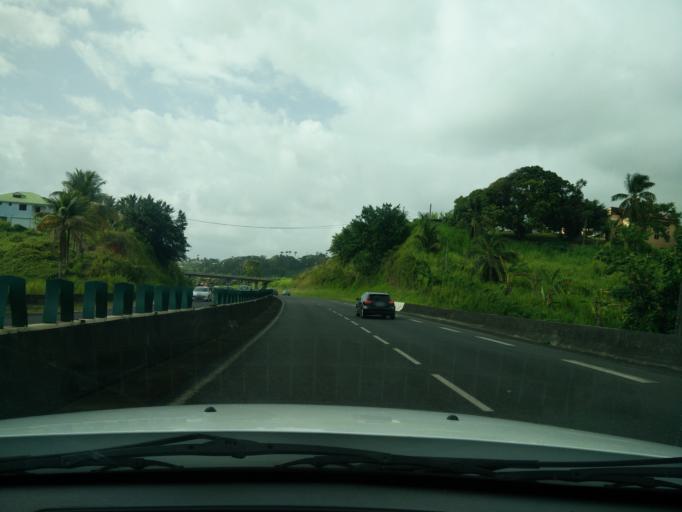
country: GP
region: Guadeloupe
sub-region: Guadeloupe
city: Petit-Bourg
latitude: 16.1865
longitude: -61.6071
